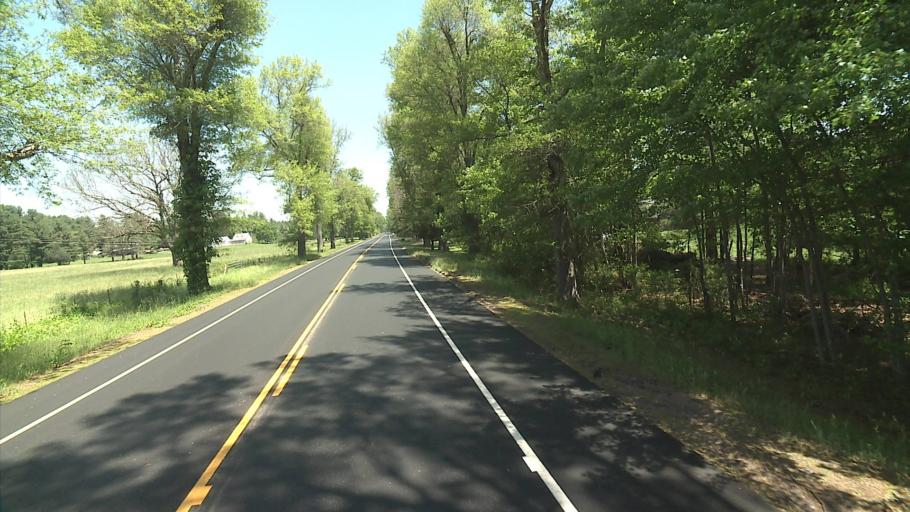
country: US
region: Connecticut
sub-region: Tolland County
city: Crystal Lake
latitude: 41.9525
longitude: -72.3707
